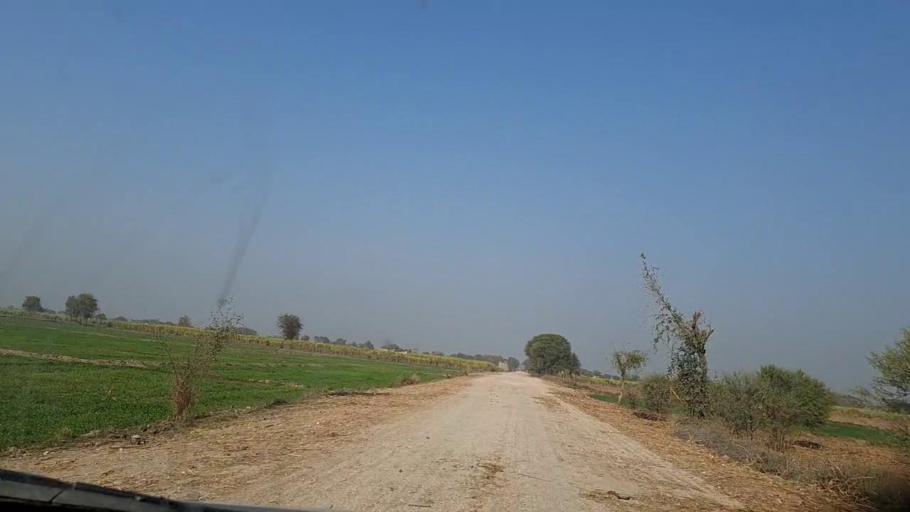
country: PK
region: Sindh
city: Moro
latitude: 26.7804
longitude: 67.9358
